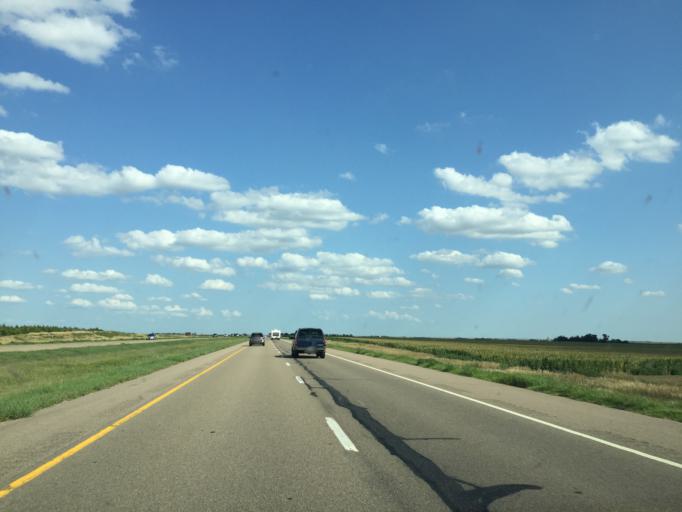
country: US
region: Kansas
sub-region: Gove County
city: Gove
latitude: 39.0377
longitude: -100.1987
